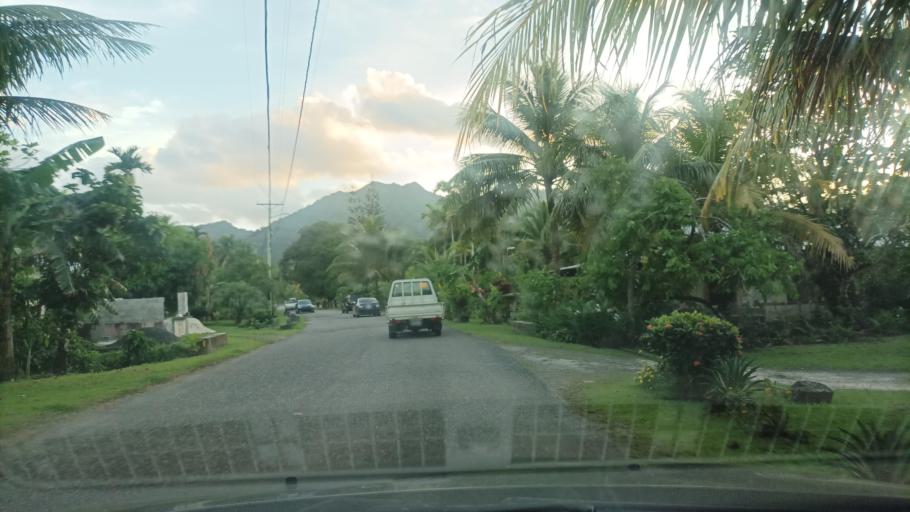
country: FM
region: Kosrae
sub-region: Lelu Municipality
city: Lelu
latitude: 5.3202
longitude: 163.0268
